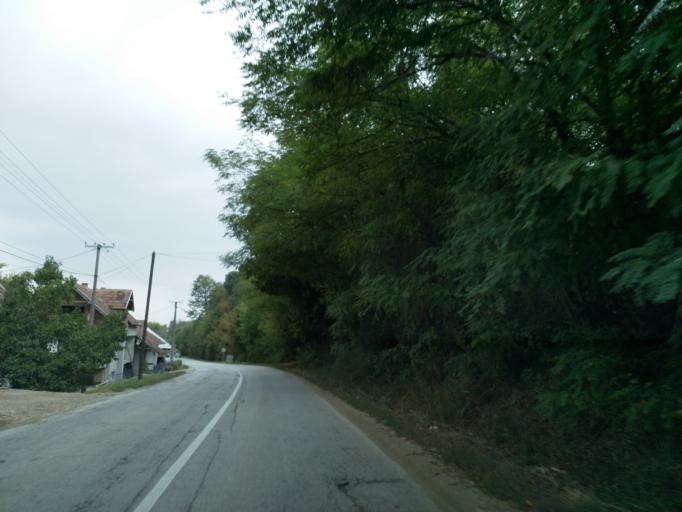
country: RS
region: Central Serbia
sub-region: Pomoravski Okrug
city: Jagodina
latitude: 44.0384
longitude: 21.1886
